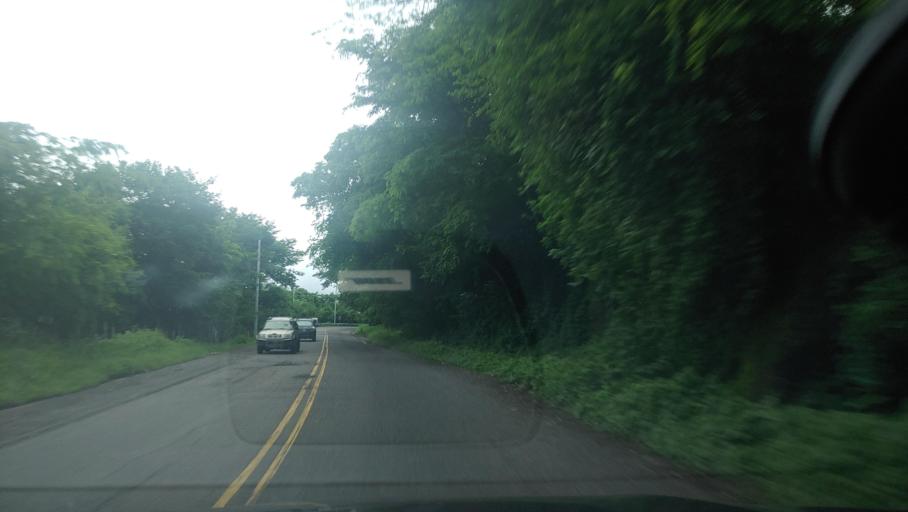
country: HN
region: Choluteca
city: Corpus
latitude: 13.3731
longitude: -87.0506
